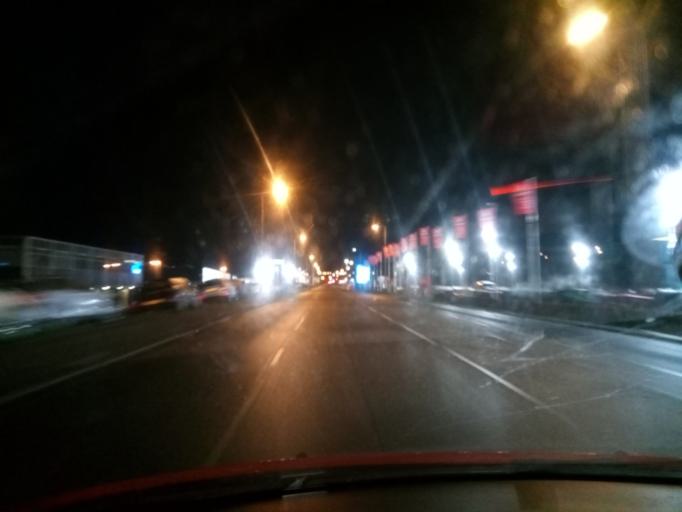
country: GB
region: Scotland
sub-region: West Lothian
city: Seafield
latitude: 55.9620
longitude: -3.1277
